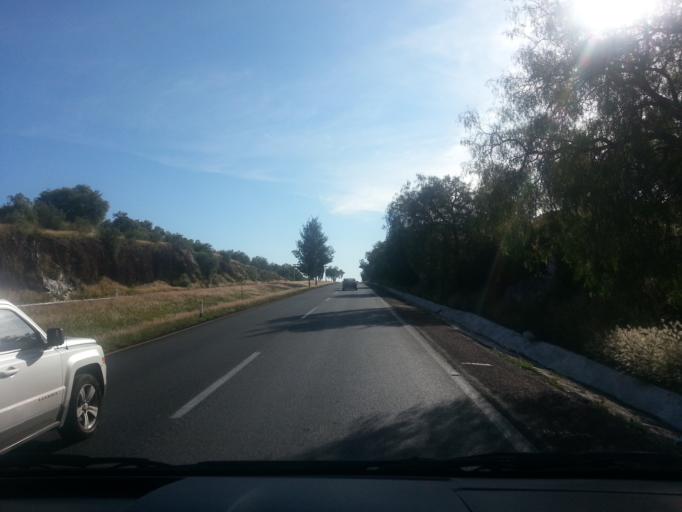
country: MX
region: Mexico
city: Acolman
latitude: 19.6209
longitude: -98.9420
